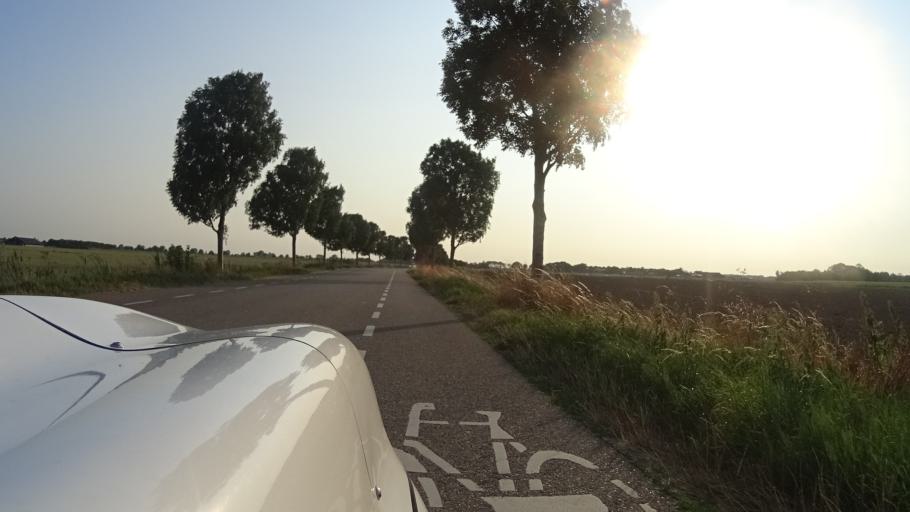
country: NL
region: North Brabant
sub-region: Gemeente Oss
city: Oss
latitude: 51.8450
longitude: 5.5285
